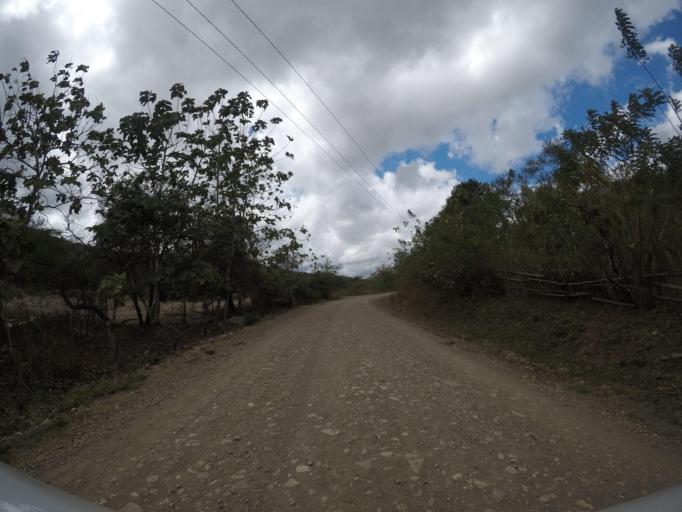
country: TL
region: Lautem
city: Lospalos
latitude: -8.5007
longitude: 126.8290
